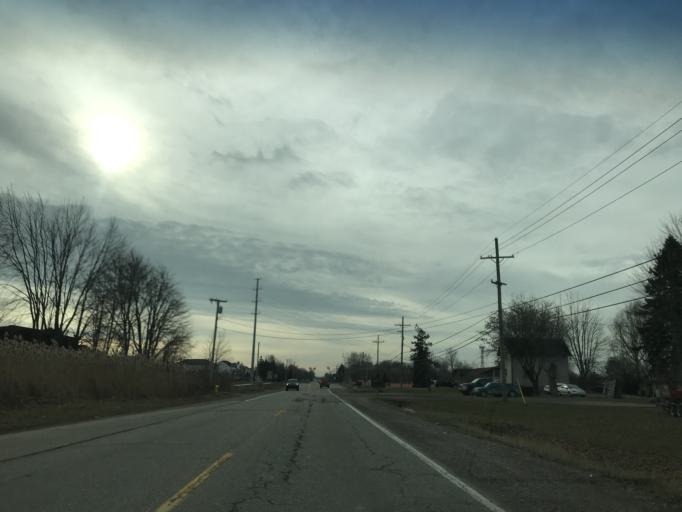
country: US
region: Michigan
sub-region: Macomb County
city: Mount Clemens
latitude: 42.6606
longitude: -82.8975
